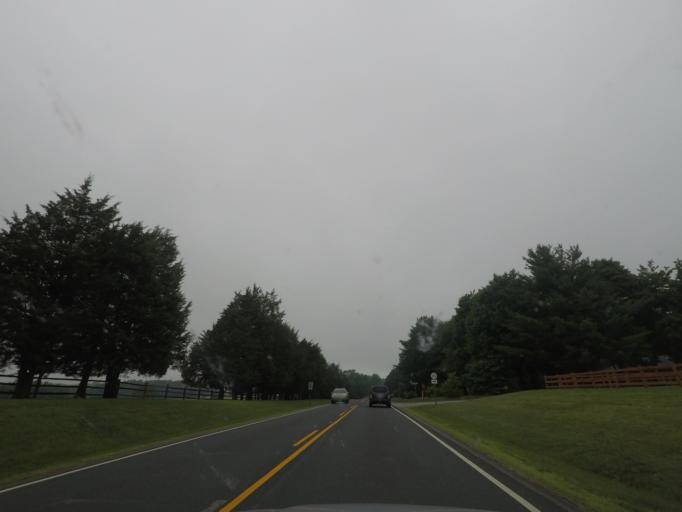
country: US
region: Virginia
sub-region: Charlotte County
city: Charlotte Court House
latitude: 37.0705
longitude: -78.4758
